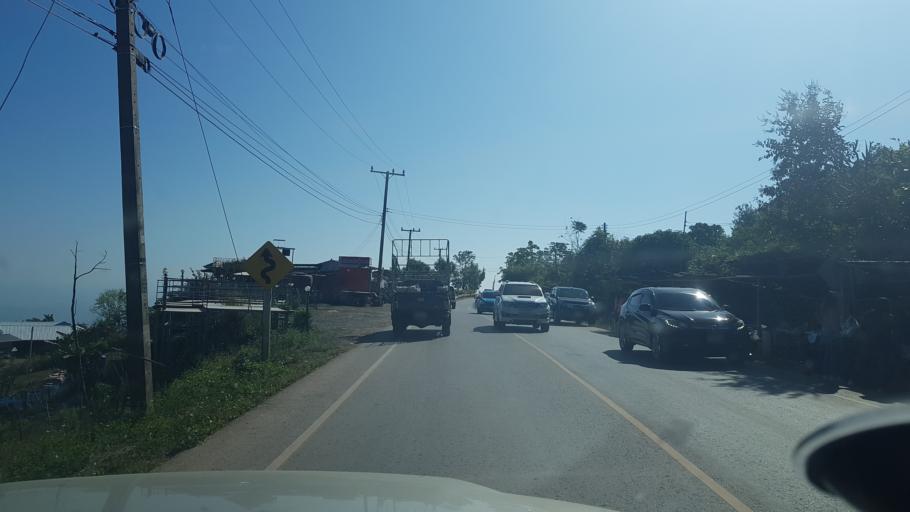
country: TH
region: Phetchabun
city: Lom Kao
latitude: 16.8788
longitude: 101.1102
